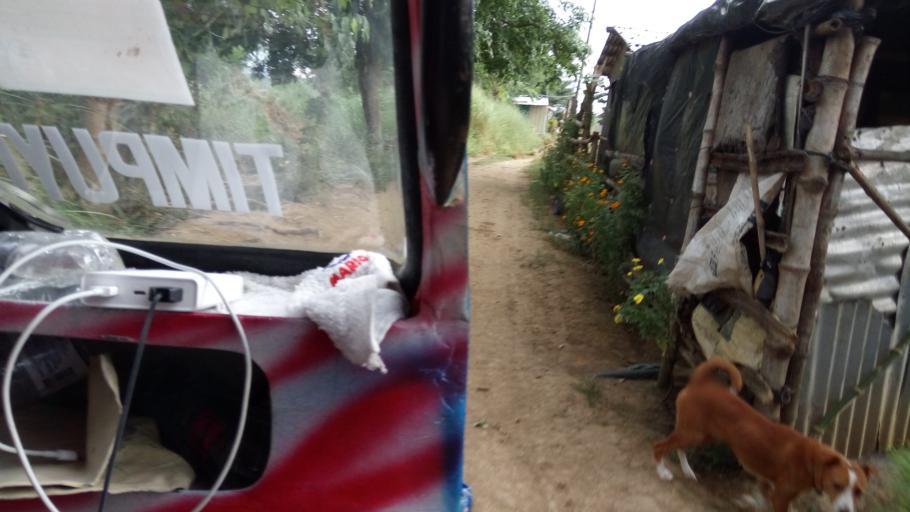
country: PH
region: Ilocos
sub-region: Province of La Union
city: Santo Tomas
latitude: 16.2755
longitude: 120.3884
